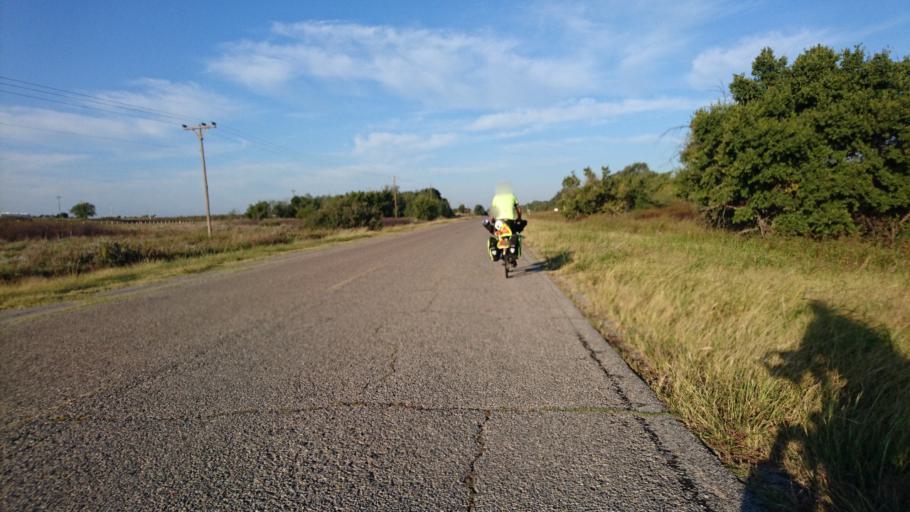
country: US
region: Oklahoma
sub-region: Beckham County
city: Sayre
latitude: 35.2618
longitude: -99.7152
